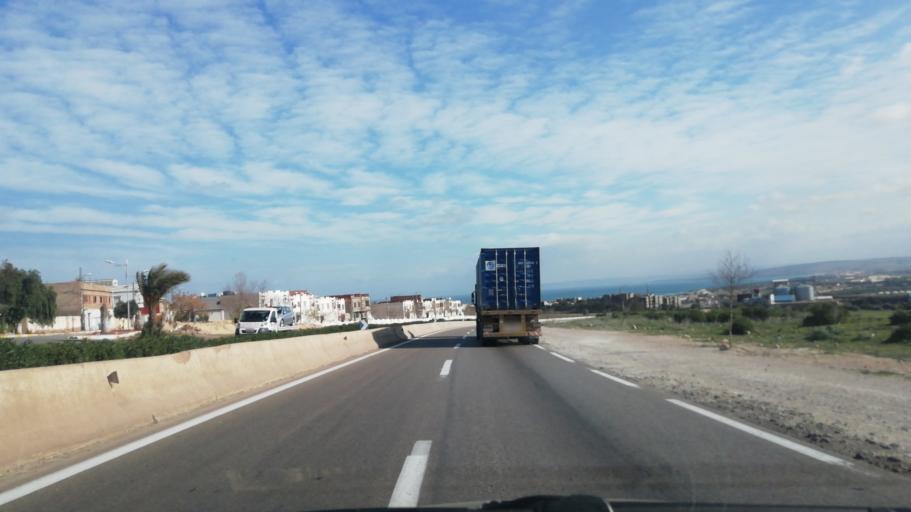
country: DZ
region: Oran
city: Ain el Bya
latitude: 35.7849
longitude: -0.1802
